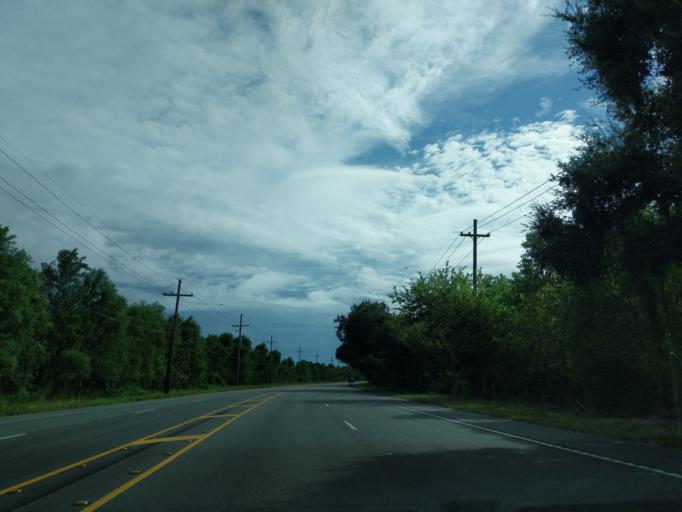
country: US
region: Louisiana
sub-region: Saint Bernard Parish
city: Meraux
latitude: 30.0669
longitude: -89.8644
